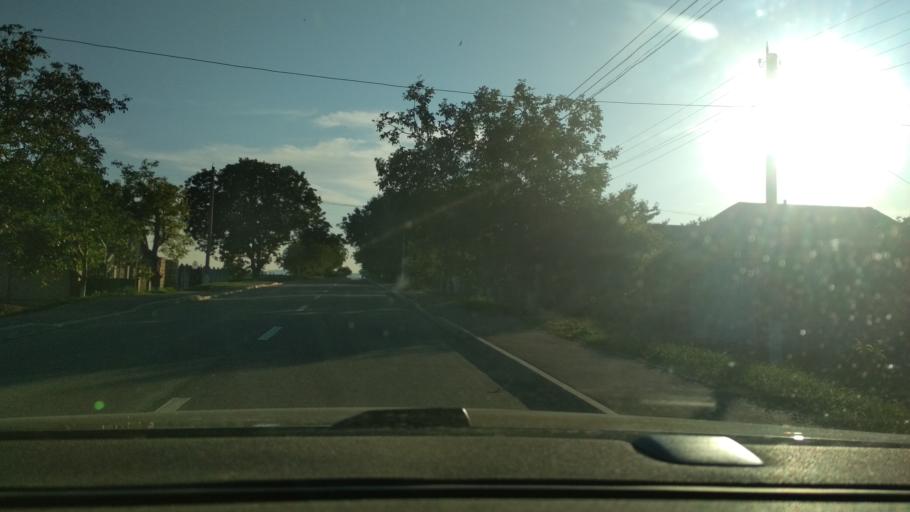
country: RO
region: Iasi
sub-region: Comuna Grozesti
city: Grozesti
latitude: 46.9635
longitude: 28.1551
